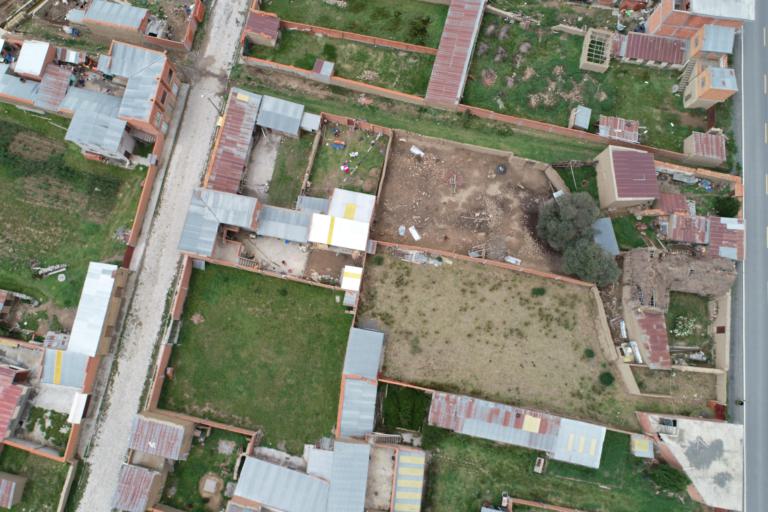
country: BO
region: La Paz
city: Huarina
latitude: -16.1899
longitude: -68.6030
